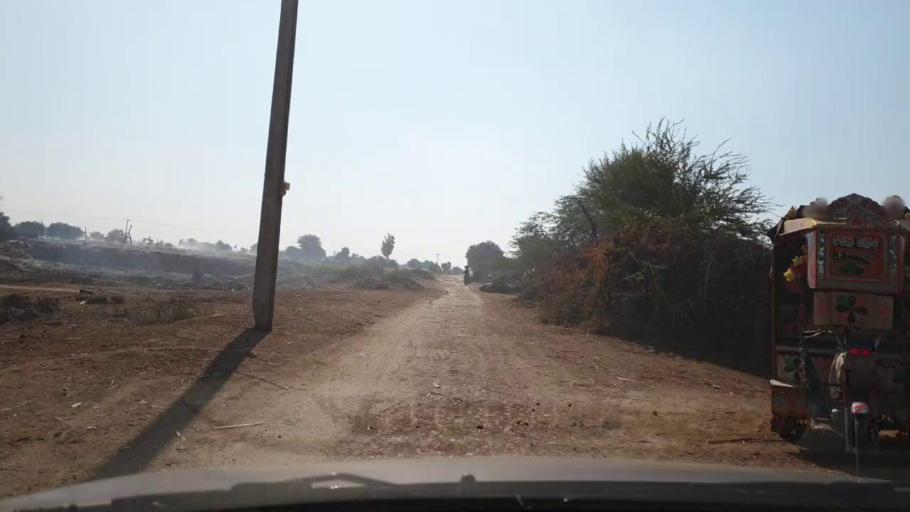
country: PK
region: Sindh
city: Jhol
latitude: 25.9380
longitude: 68.8001
